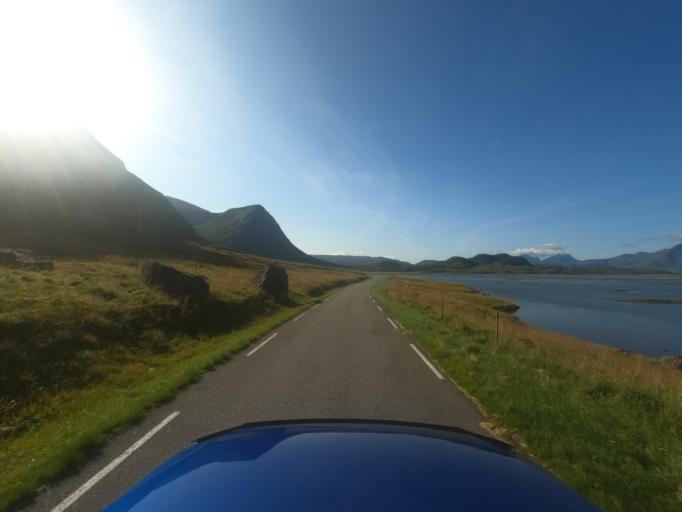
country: NO
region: Nordland
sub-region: Vestvagoy
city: Evjen
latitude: 68.3334
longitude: 13.9201
